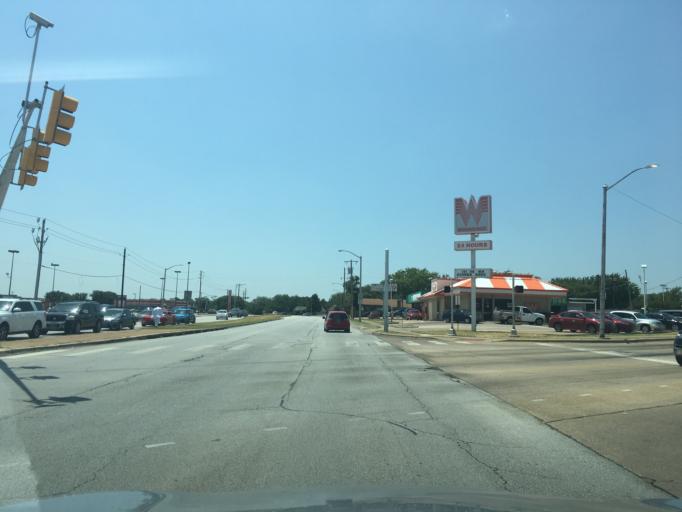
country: US
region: Texas
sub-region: Tarrant County
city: Edgecliff Village
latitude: 32.6498
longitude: -97.3677
